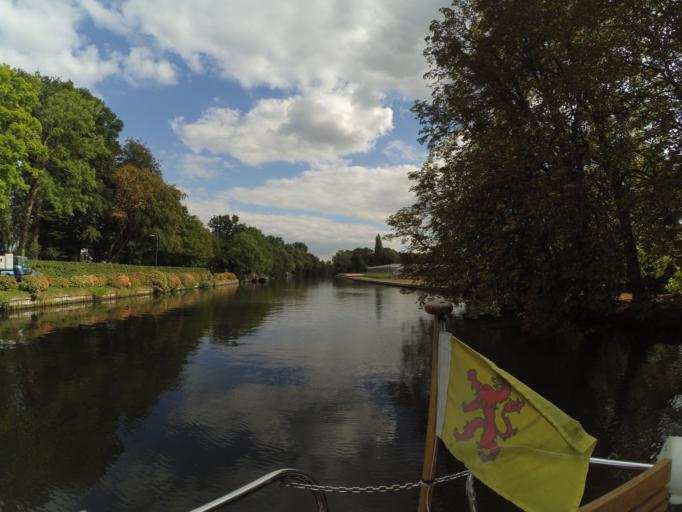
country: NL
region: Utrecht
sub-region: Stichtse Vecht
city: Breukelen
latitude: 52.1604
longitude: 5.0134
